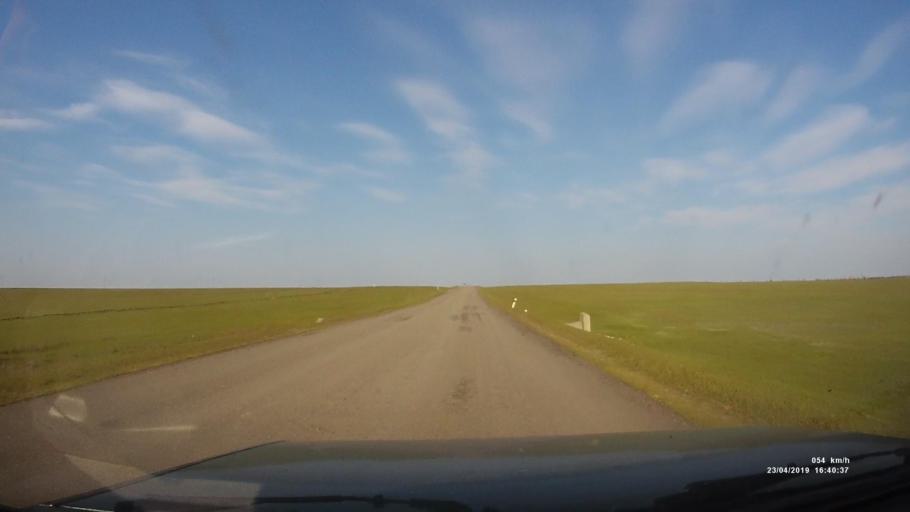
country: RU
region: Kalmykiya
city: Priyutnoye
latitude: 46.3434
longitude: 43.1782
